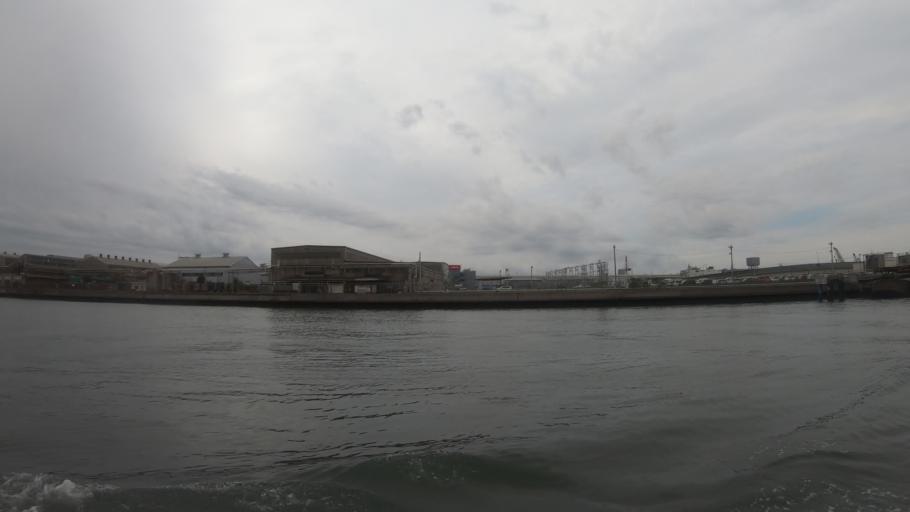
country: JP
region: Kanagawa
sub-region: Kawasaki-shi
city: Kawasaki
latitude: 35.4877
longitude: 139.6791
